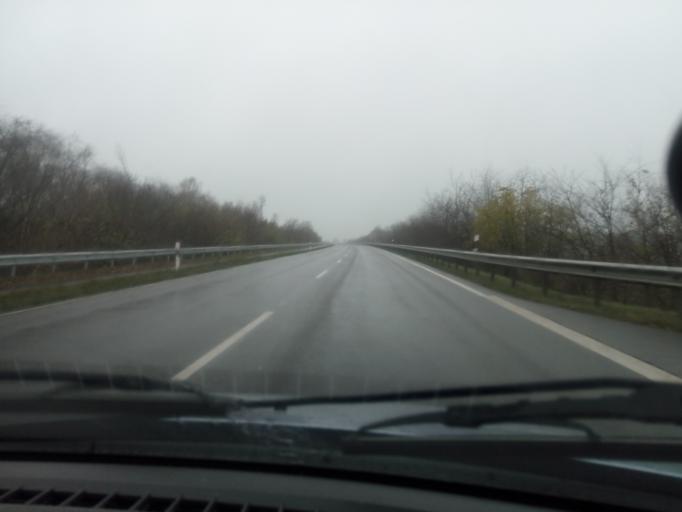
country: DE
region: Lower Saxony
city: Lehe
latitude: 52.9906
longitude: 7.3574
